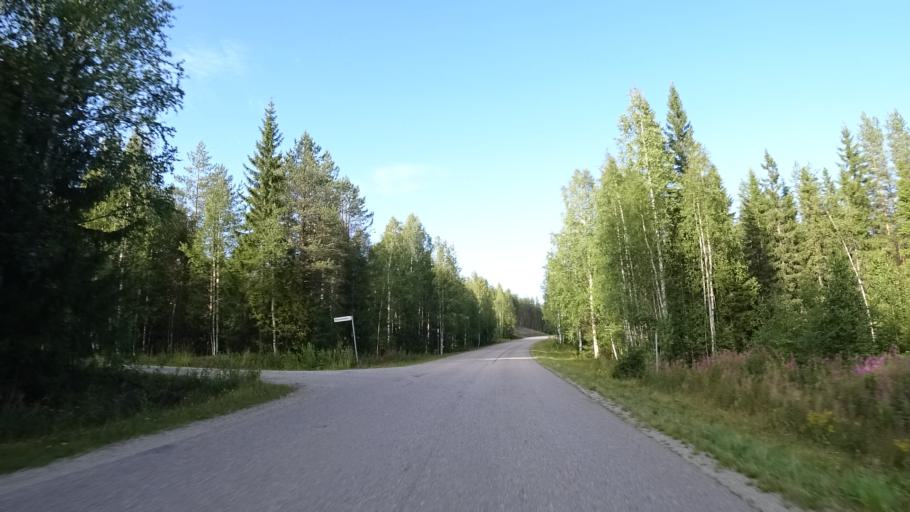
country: FI
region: North Karelia
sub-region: Joensuu
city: Eno
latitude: 63.0254
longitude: 30.5028
